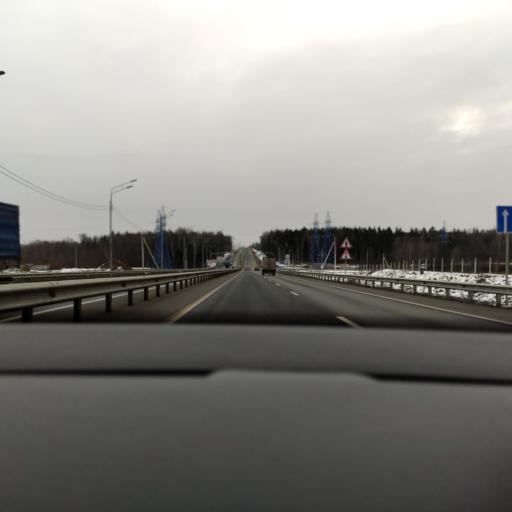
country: RU
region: Moskovskaya
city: Zvenigorod
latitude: 55.6898
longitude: 36.8850
